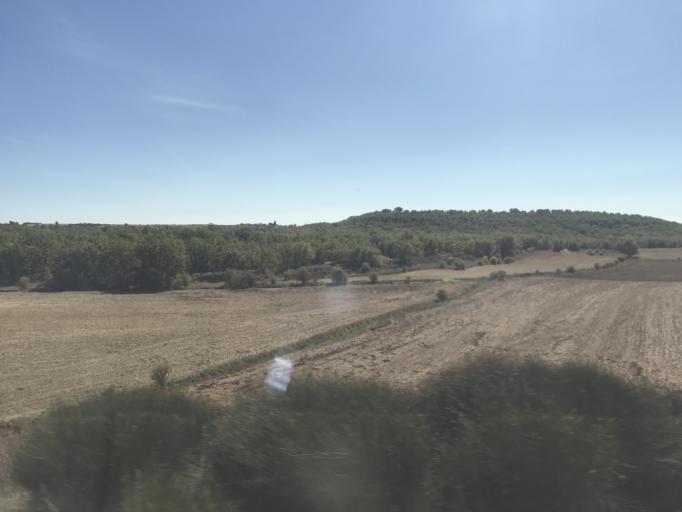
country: ES
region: Castille-La Mancha
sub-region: Provincia de Guadalajara
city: Torremocha del Campo
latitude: 40.9406
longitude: -2.6170
